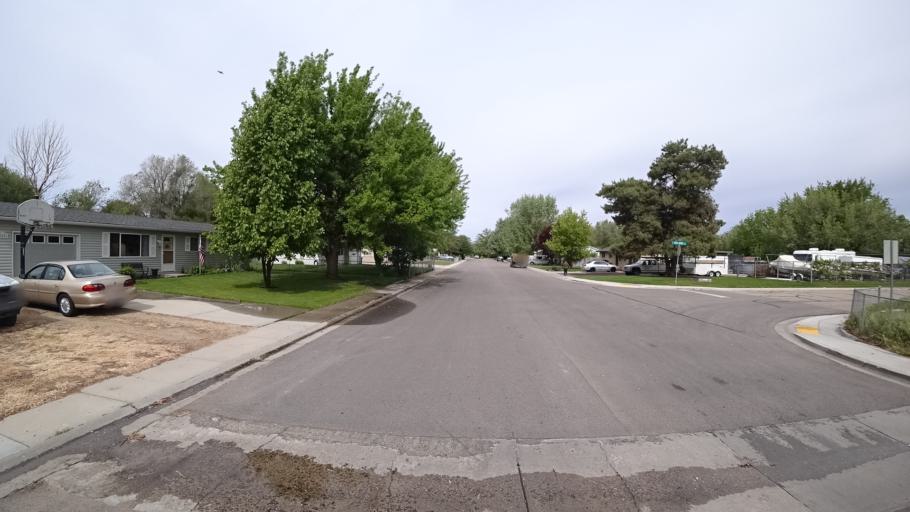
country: US
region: Idaho
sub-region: Ada County
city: Garden City
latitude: 43.5348
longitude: -116.3071
